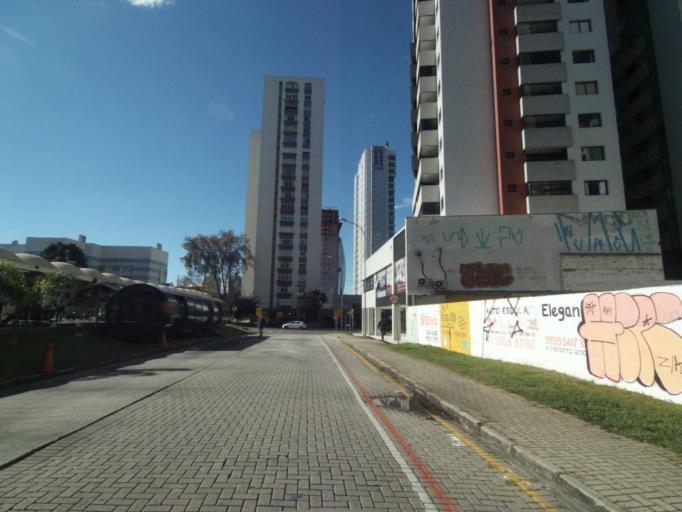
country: BR
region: Parana
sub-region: Curitiba
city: Curitiba
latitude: -25.4068
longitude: -49.2523
